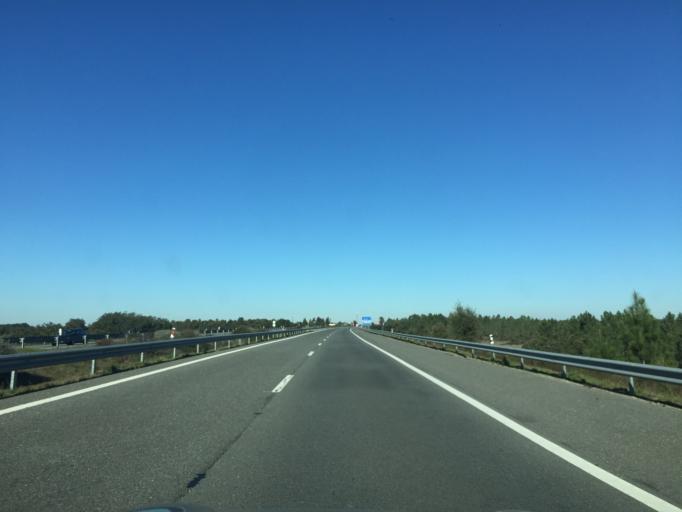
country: PT
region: Setubal
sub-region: Grandola
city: Grandola
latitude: 38.1610
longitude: -8.4834
